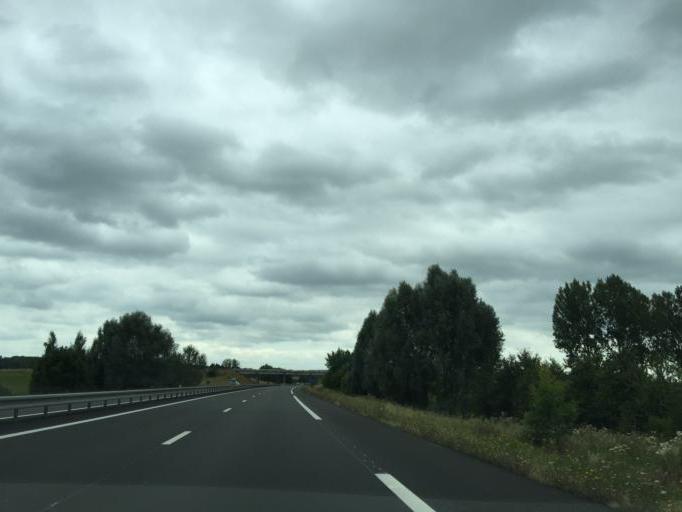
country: FR
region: Pays de la Loire
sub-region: Departement de la Sarthe
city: Brette-les-Pins
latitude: 47.9044
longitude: 0.3038
